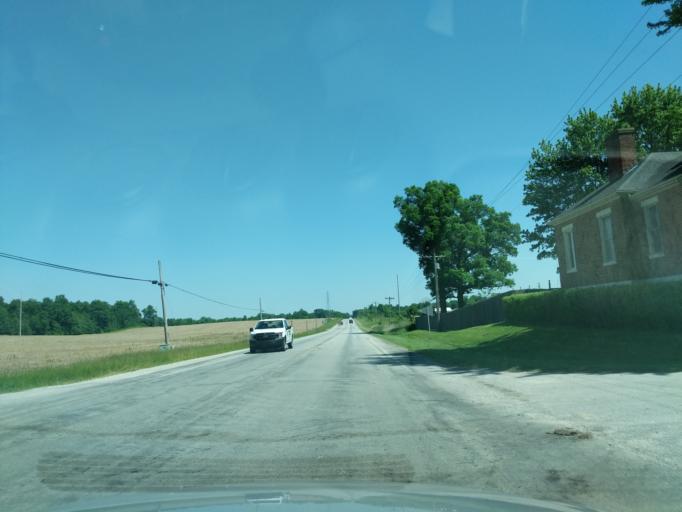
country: US
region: Indiana
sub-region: Whitley County
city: Columbia City
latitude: 41.1037
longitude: -85.4714
